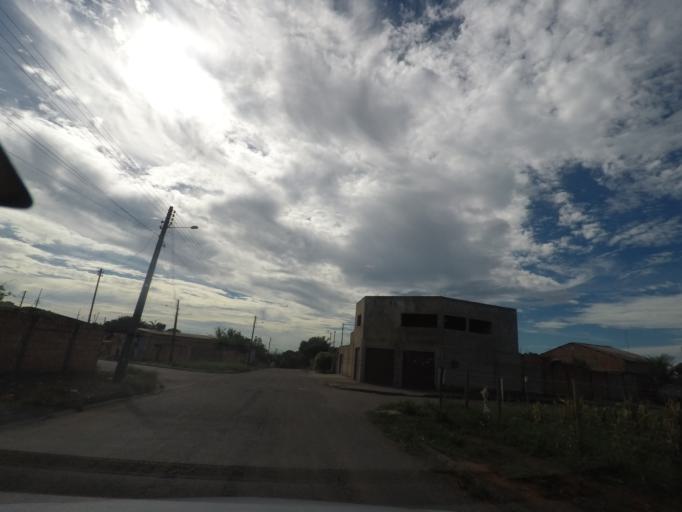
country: BR
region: Goias
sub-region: Aparecida De Goiania
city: Aparecida de Goiania
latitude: -16.8337
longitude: -49.2969
